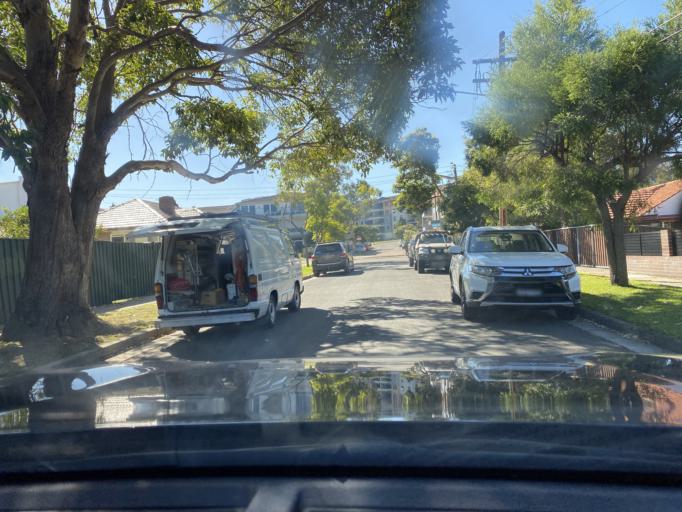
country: AU
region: New South Wales
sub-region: Canada Bay
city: Wareemba
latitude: -33.8526
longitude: 151.1340
